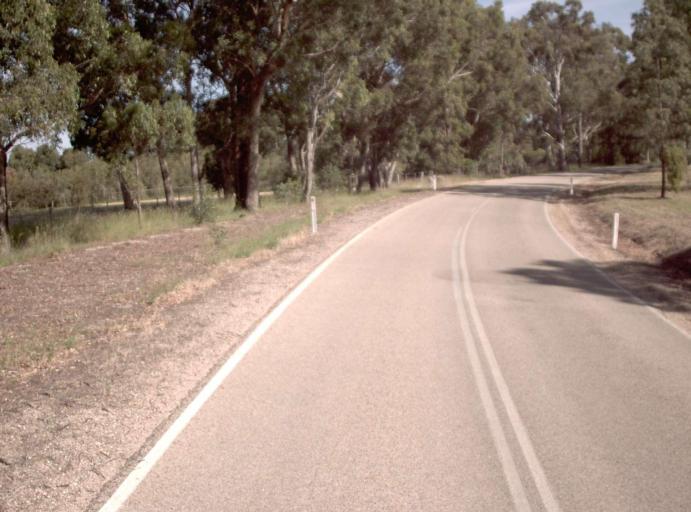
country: AU
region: Victoria
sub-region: East Gippsland
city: Lakes Entrance
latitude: -37.7724
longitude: 147.8135
